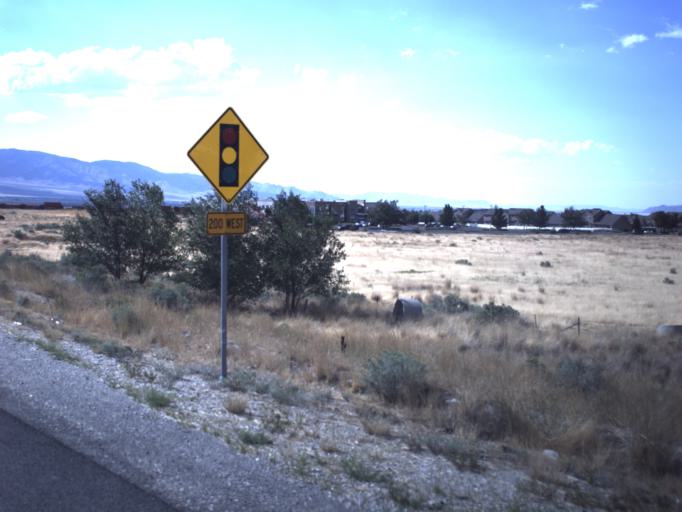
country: US
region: Utah
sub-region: Tooele County
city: Tooele
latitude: 40.5510
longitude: -112.3001
